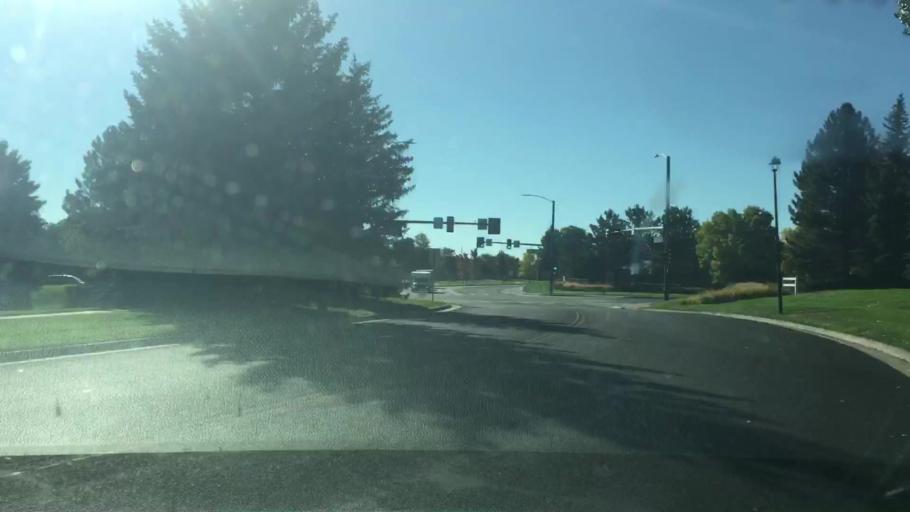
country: US
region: Colorado
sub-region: Douglas County
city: Stonegate
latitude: 39.5181
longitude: -104.7867
